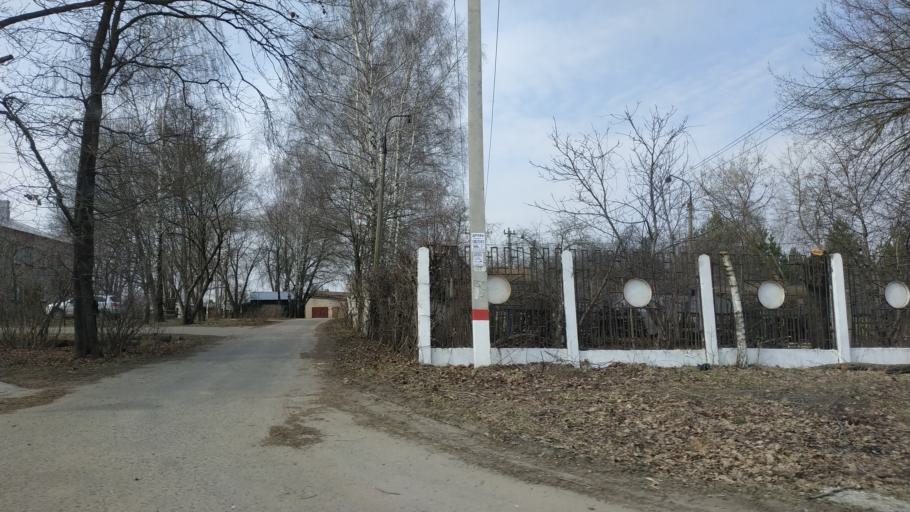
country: RU
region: Moskovskaya
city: Bronnitsy
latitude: 55.3907
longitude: 38.3511
